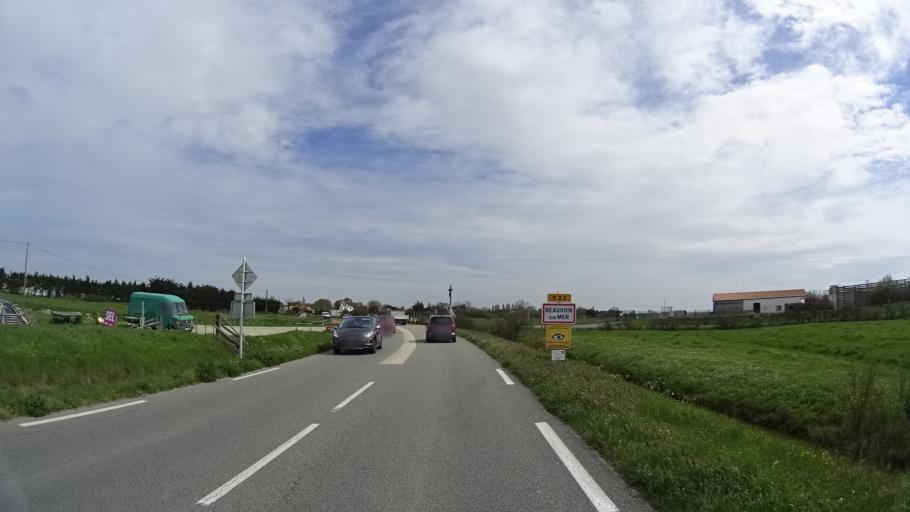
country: FR
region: Pays de la Loire
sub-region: Departement de la Vendee
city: Beauvoir-sur-Mer
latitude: 46.9046
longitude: -2.0522
